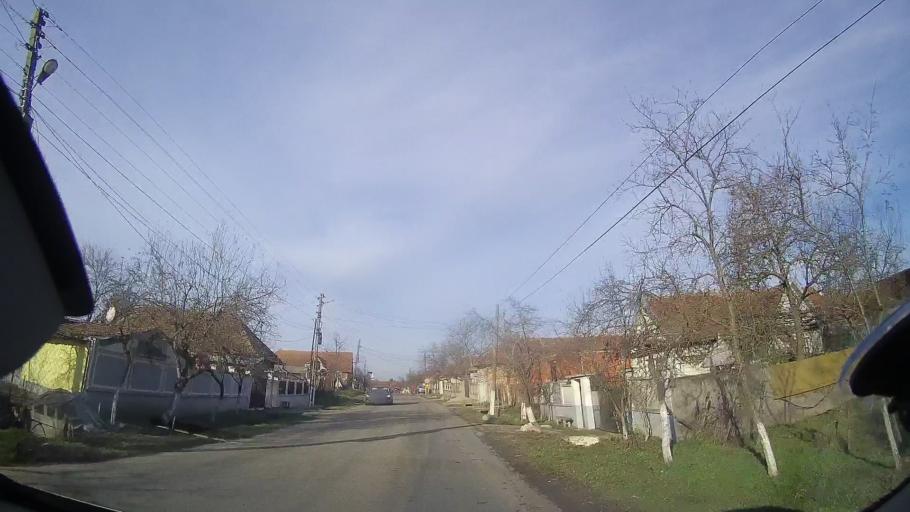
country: RO
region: Bihor
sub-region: Comuna Brusturi
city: Brusturi
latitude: 47.1688
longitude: 22.2202
